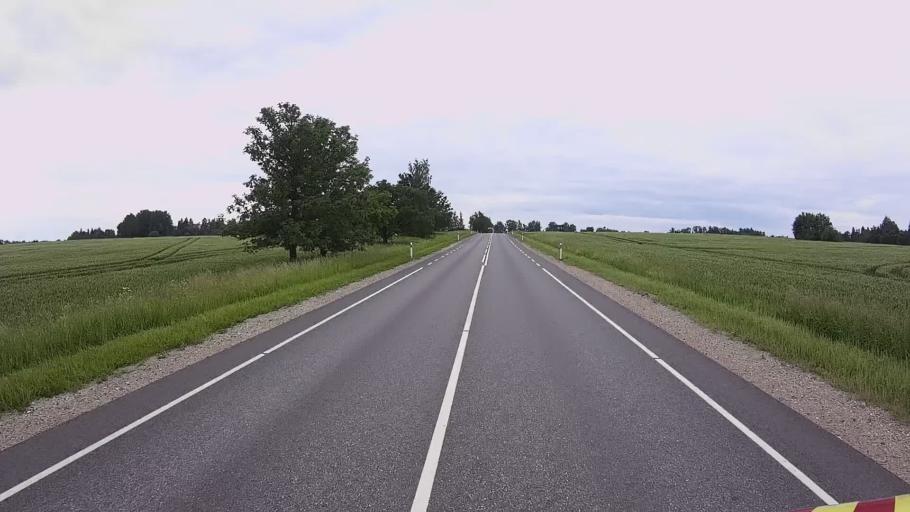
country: EE
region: Viljandimaa
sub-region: Karksi vald
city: Karksi-Nuia
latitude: 58.1388
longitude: 25.5857
